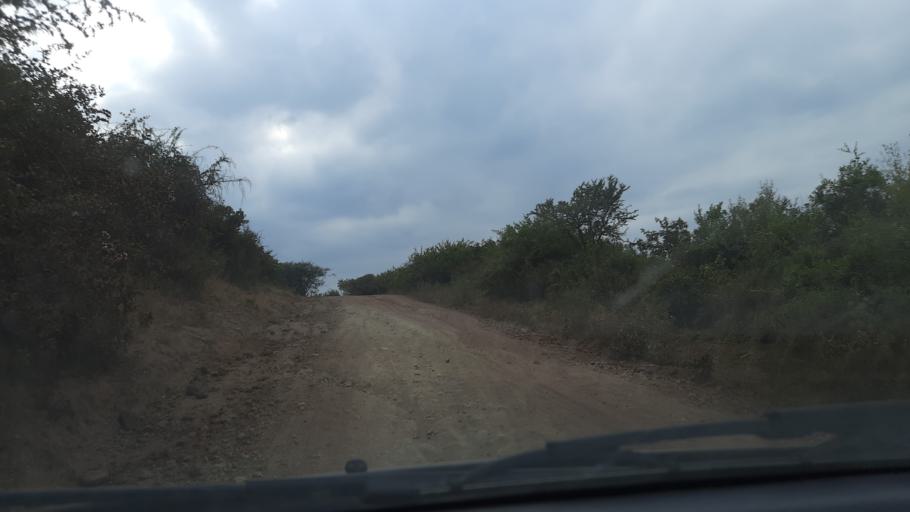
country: TZ
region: Kilimanjaro
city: Moshi
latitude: -2.8587
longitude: 37.2751
